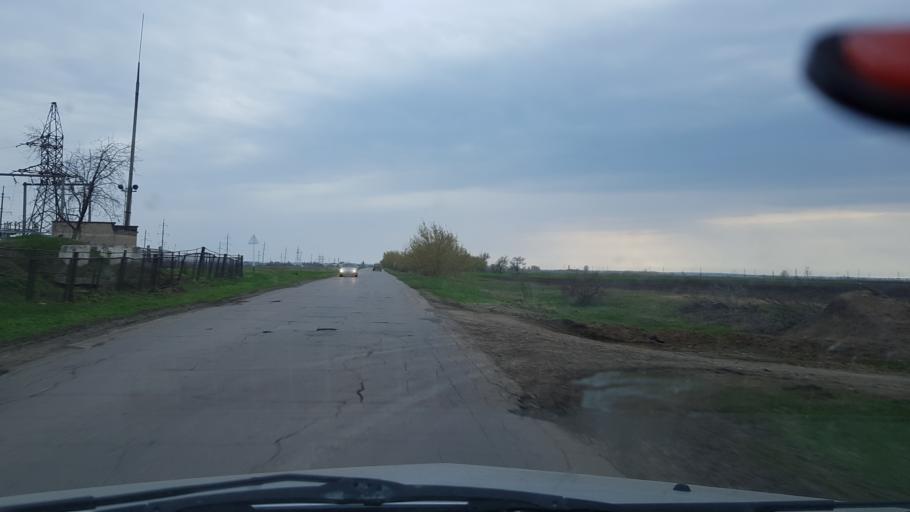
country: RU
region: Samara
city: Khryashchevka
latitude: 53.6706
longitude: 49.1094
